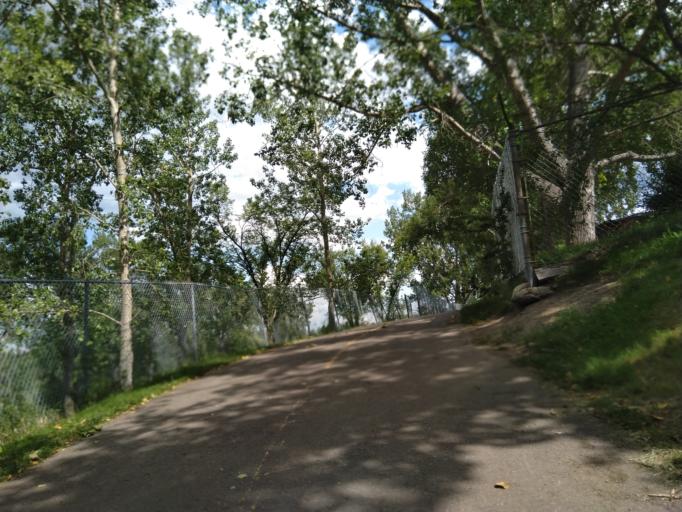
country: CA
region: Alberta
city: Calgary
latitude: 51.0770
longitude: -114.1005
